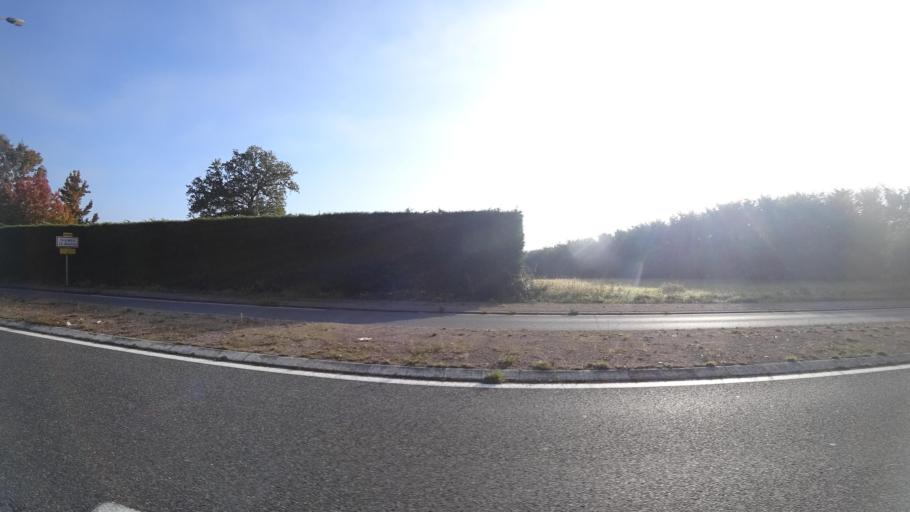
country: FR
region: Midi-Pyrenees
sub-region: Departement de l'Aveyron
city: Olemps
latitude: 44.3246
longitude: 2.5587
